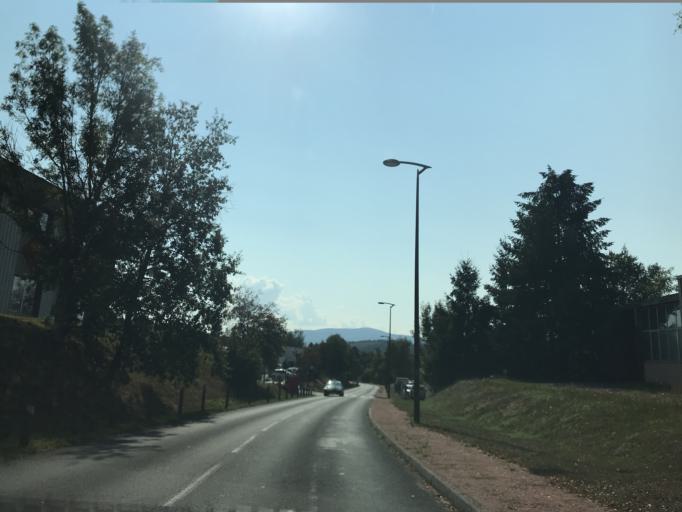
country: FR
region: Auvergne
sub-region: Departement du Puy-de-Dome
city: La Monnerie-le-Montel
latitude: 45.8800
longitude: 3.6214
